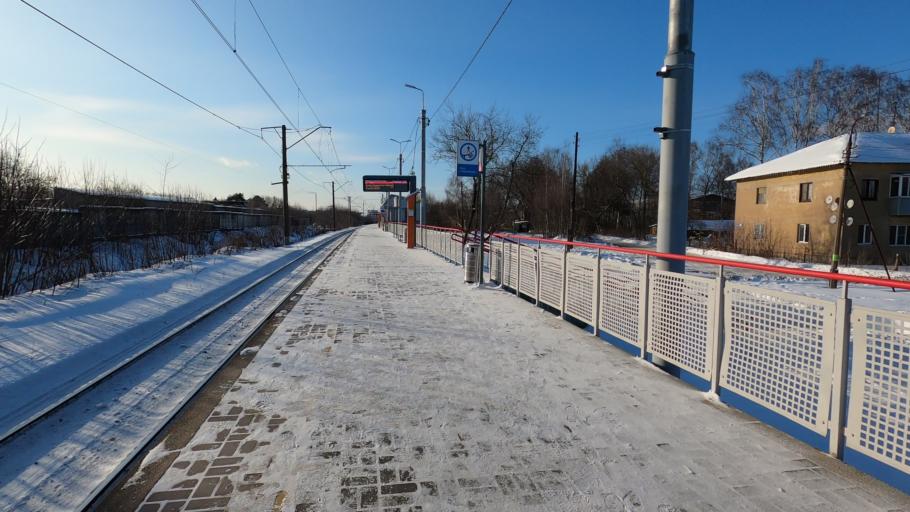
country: RU
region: Moskovskaya
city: Pavlovskiy Posad
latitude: 55.7744
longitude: 38.7010
